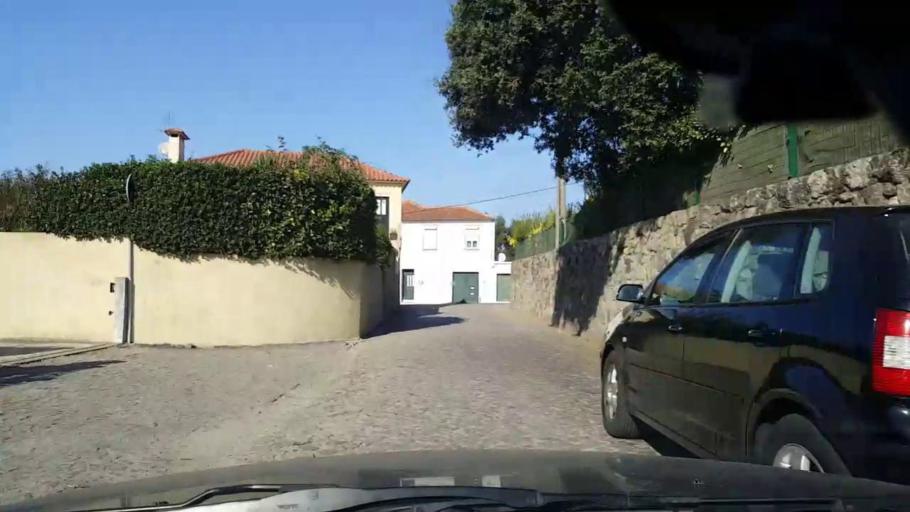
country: PT
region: Porto
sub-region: Vila do Conde
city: Arvore
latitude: 41.3565
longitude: -8.7180
